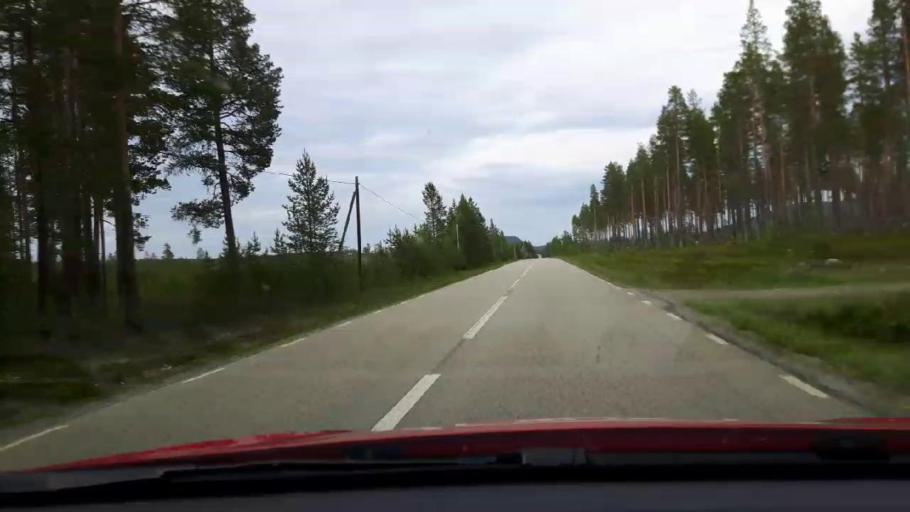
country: SE
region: Jaemtland
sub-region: Bergs Kommun
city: Hoverberg
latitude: 62.6485
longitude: 14.0830
